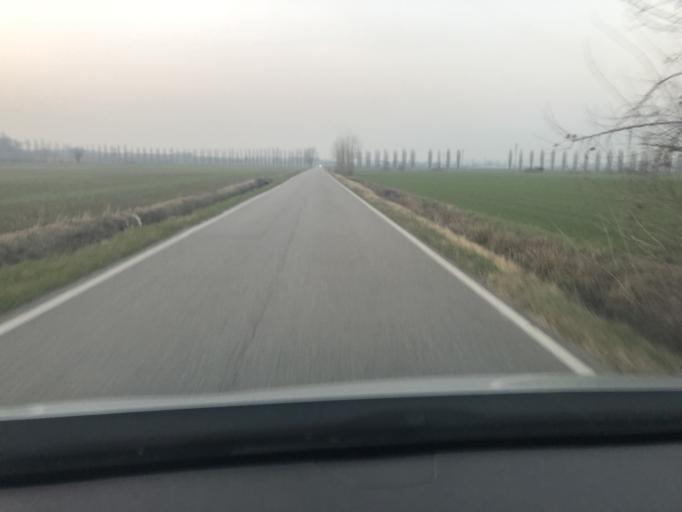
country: IT
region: Veneto
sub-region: Provincia di Verona
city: San Giorgio in Salici
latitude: 45.4002
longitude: 10.8002
